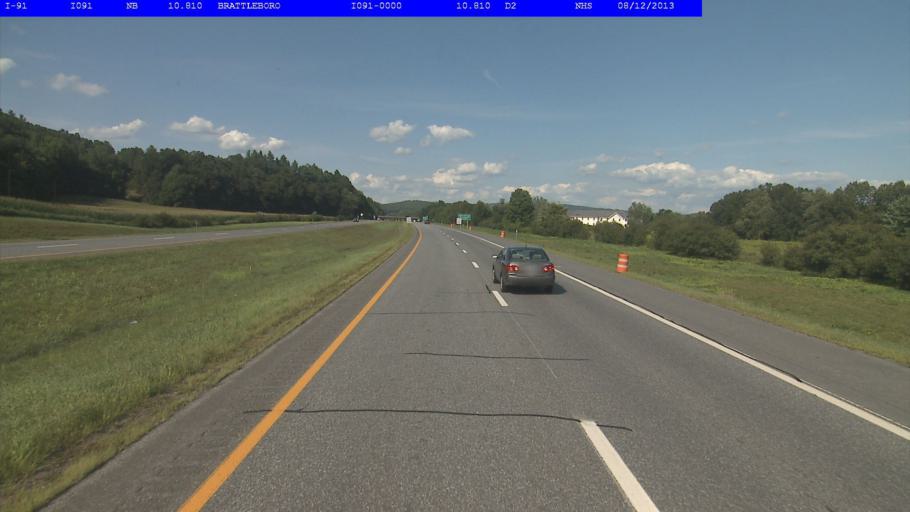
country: US
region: Vermont
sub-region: Windham County
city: Brattleboro
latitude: 42.8770
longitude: -72.5673
